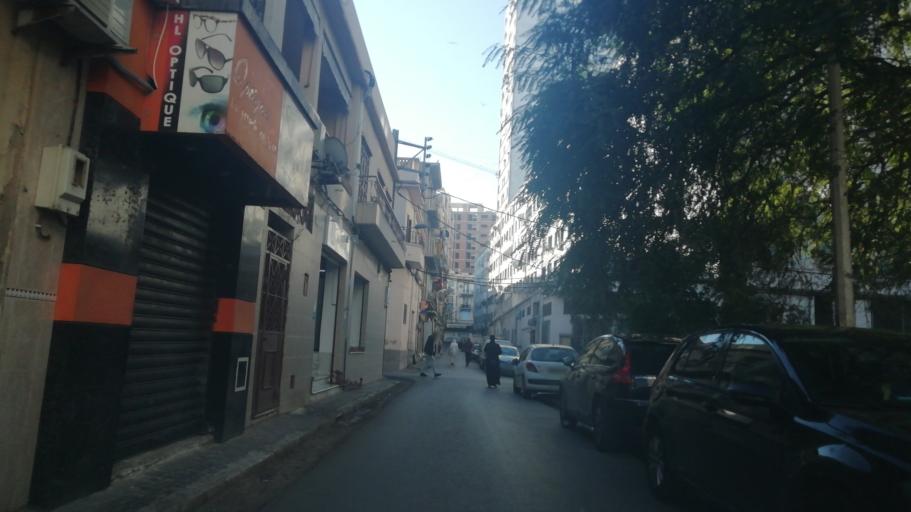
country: DZ
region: Oran
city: Oran
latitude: 35.7055
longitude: -0.6343
